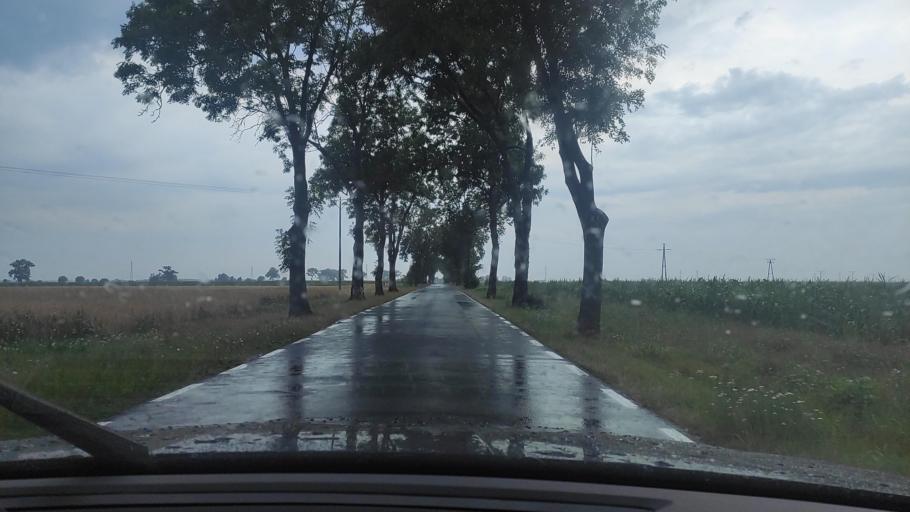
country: PL
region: Greater Poland Voivodeship
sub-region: Powiat poznanski
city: Kleszczewo
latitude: 52.2902
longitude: 17.1833
